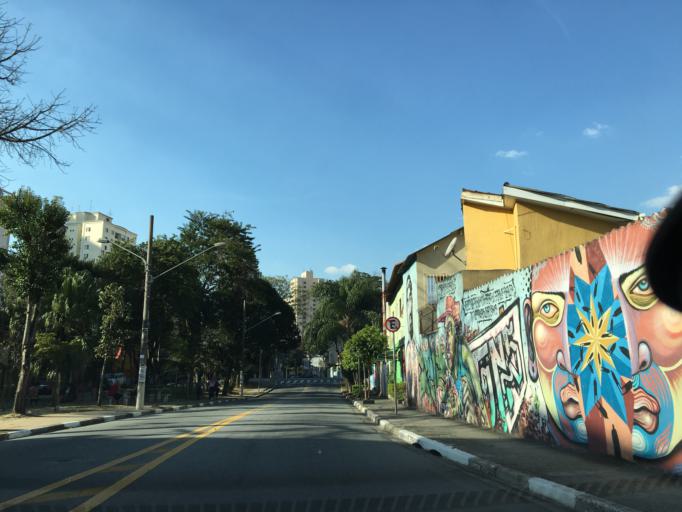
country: BR
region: Sao Paulo
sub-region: Sao Paulo
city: Sao Paulo
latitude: -23.4747
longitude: -46.6375
